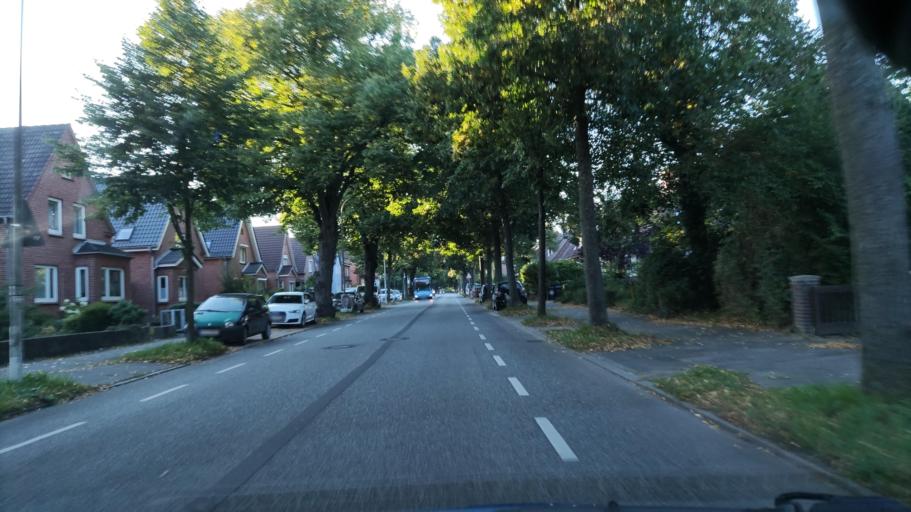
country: DE
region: Schleswig-Holstein
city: Klausdorf
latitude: 54.3225
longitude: 10.1996
